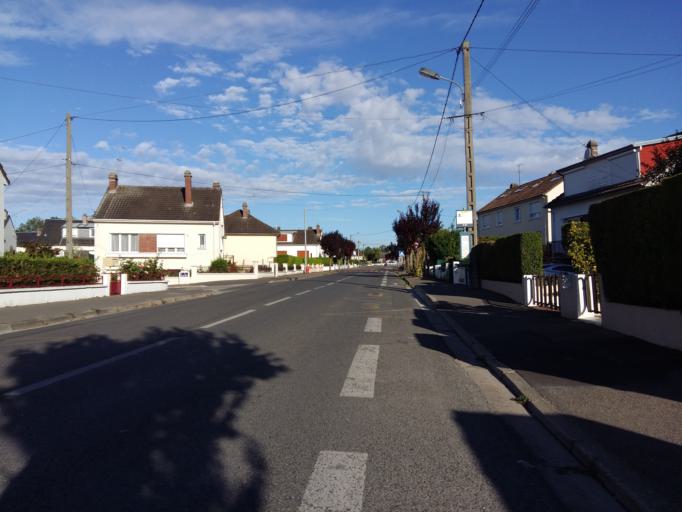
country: FR
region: Picardie
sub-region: Departement de la Somme
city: Rivery
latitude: 49.9033
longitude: 2.3295
